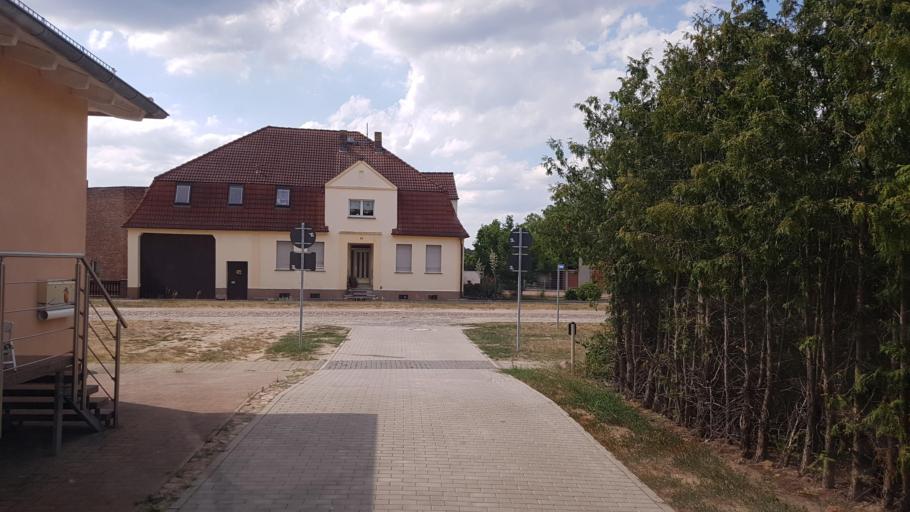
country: DE
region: Brandenburg
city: Golzow
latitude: 52.3169
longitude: 12.5608
